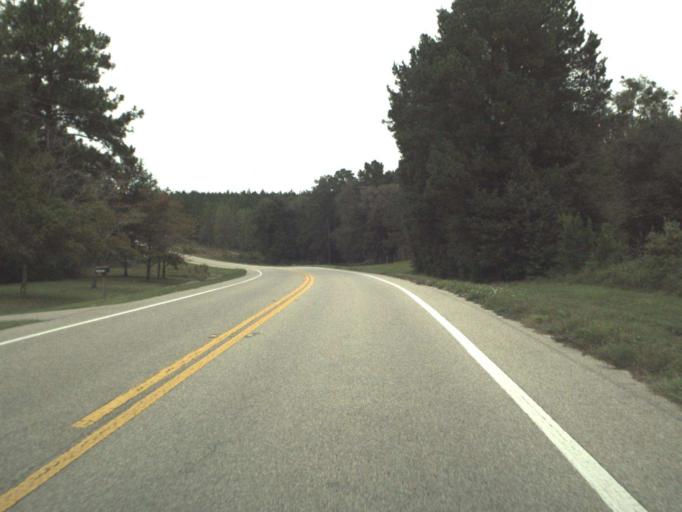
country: US
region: Florida
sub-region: Calhoun County
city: Blountstown
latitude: 30.5830
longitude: -85.0219
